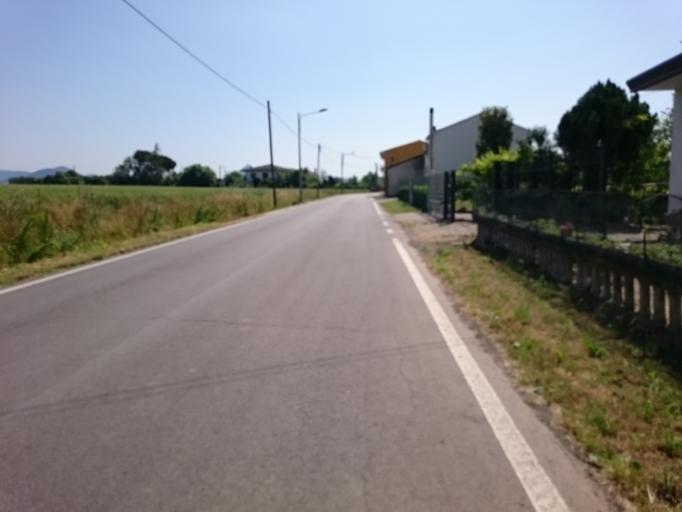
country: IT
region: Veneto
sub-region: Provincia di Padova
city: Saletto
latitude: 45.2508
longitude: 11.5577
